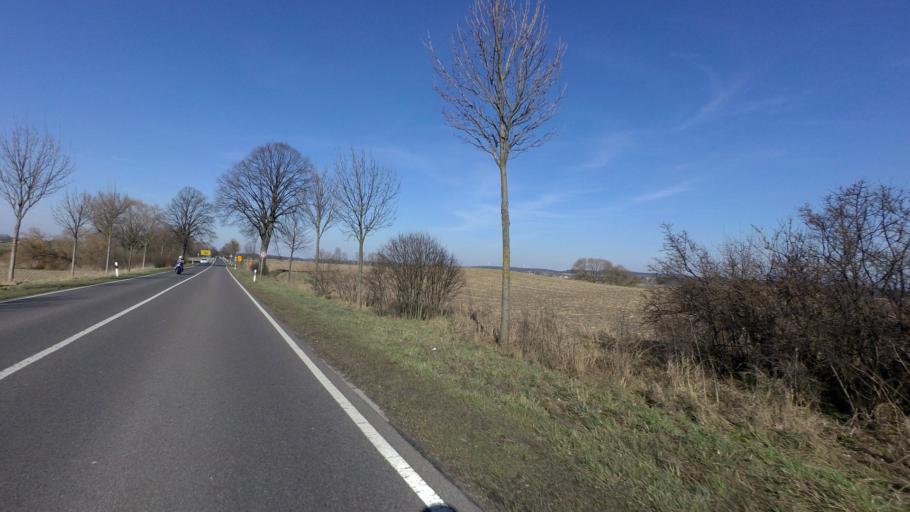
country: DE
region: Brandenburg
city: Angermunde
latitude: 52.9685
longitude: 13.9642
